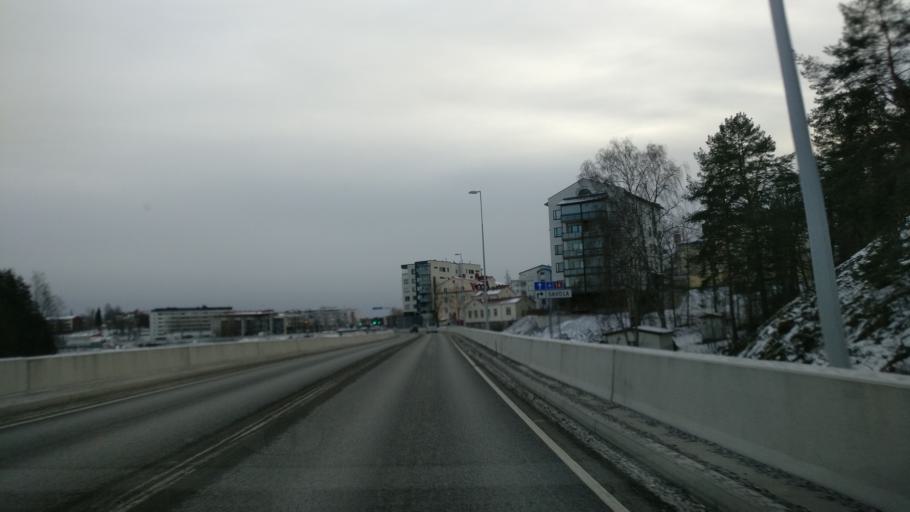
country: FI
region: Southern Savonia
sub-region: Savonlinna
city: Savonlinna
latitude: 61.8726
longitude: 28.8813
